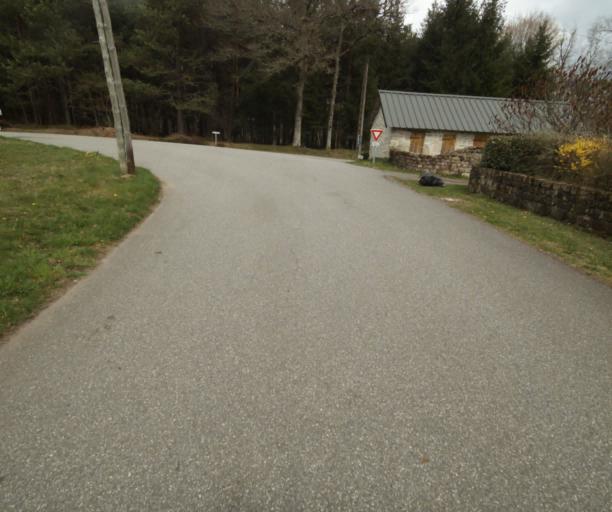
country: FR
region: Limousin
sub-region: Departement de la Correze
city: Correze
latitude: 45.3341
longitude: 1.9212
